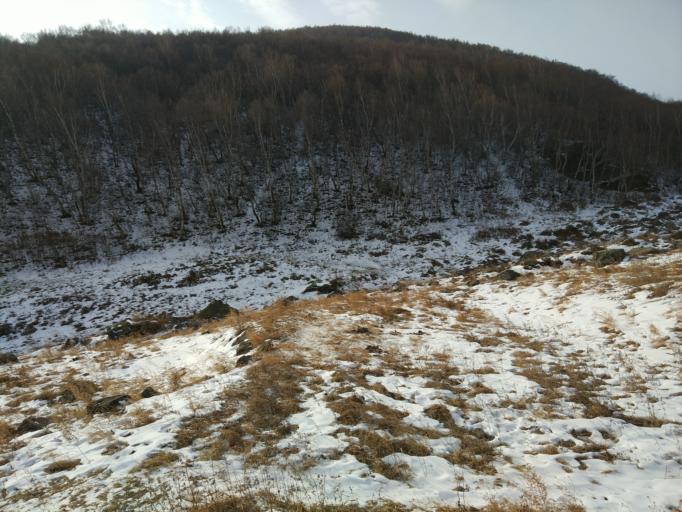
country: CN
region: Hebei
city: Xiwanzi
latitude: 40.8541
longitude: 115.4584
